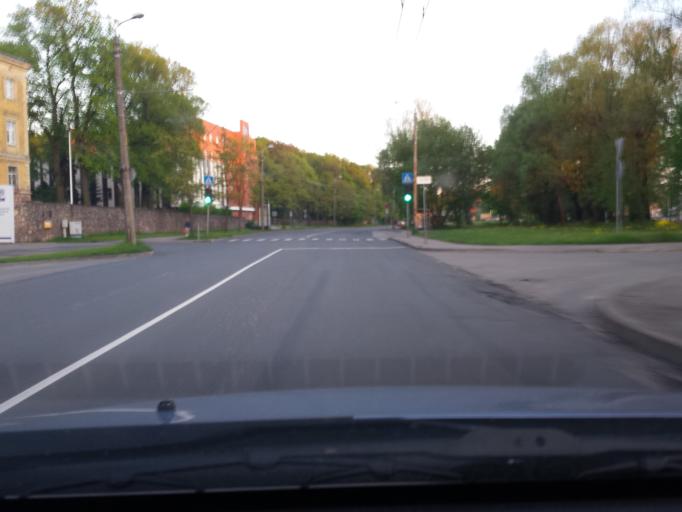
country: LV
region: Riga
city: Riga
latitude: 56.9837
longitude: 24.1360
